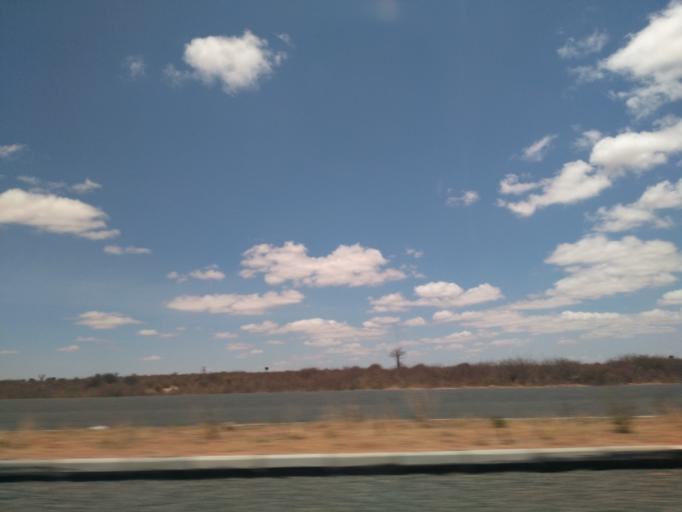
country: TZ
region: Dodoma
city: Kisasa
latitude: -6.1718
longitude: 35.8367
